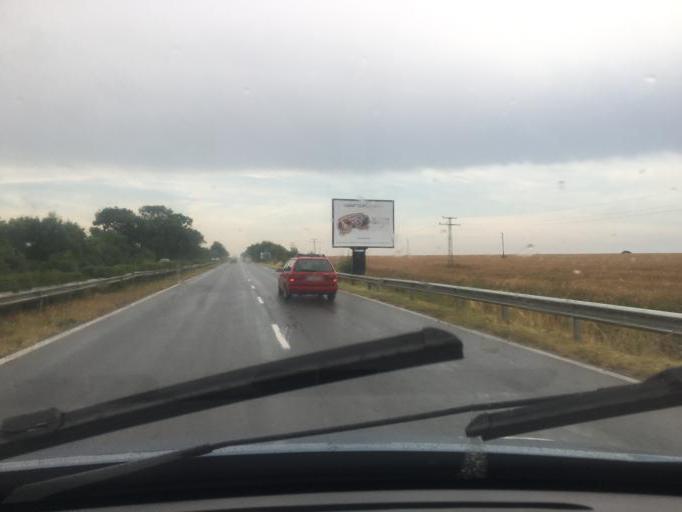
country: BG
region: Burgas
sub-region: Obshtina Burgas
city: Burgas
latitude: 42.5529
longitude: 27.4971
